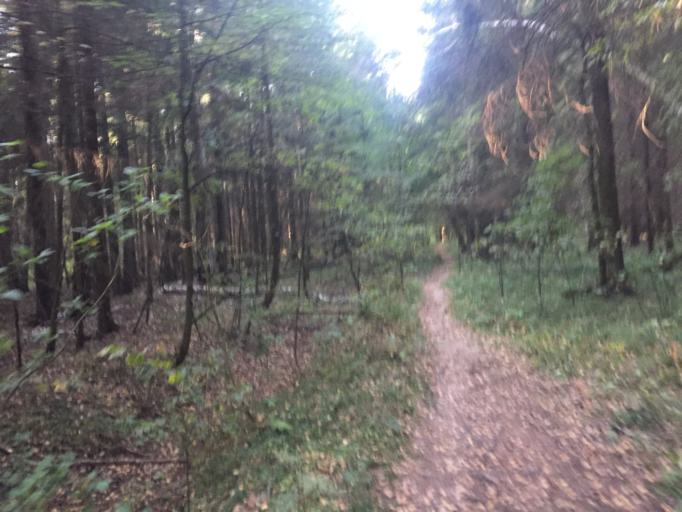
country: RU
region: Moscow
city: Metrogorodok
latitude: 55.8439
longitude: 37.7706
